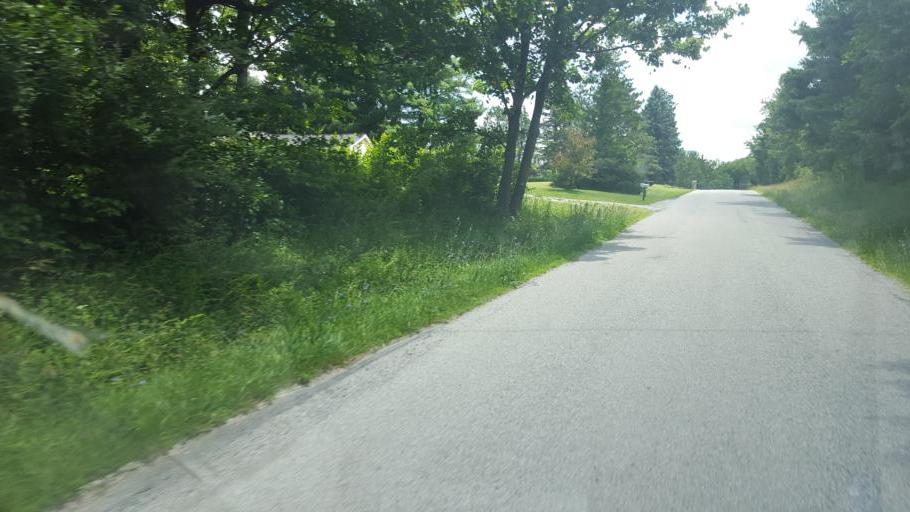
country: US
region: Ohio
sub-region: Richland County
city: Ontario
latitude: 40.7394
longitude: -82.6265
